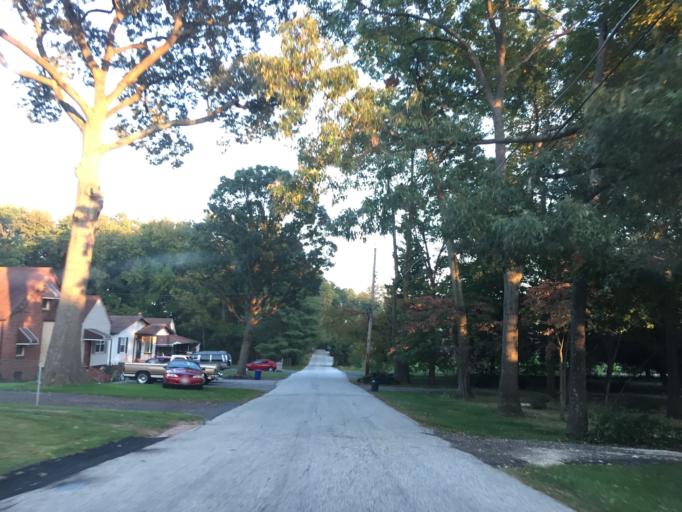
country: US
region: Maryland
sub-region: Baltimore County
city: Essex
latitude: 39.3202
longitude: -76.4623
